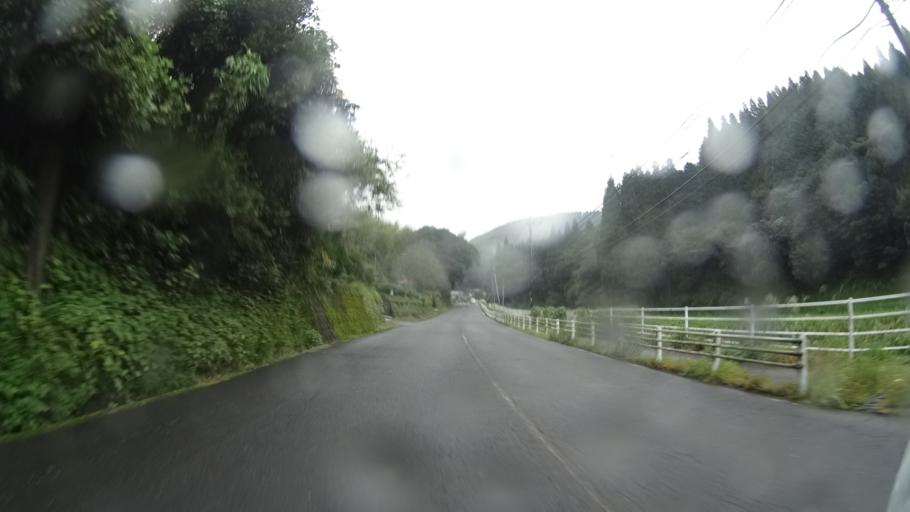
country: JP
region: Kagoshima
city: Kajiki
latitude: 31.8230
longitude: 130.6783
